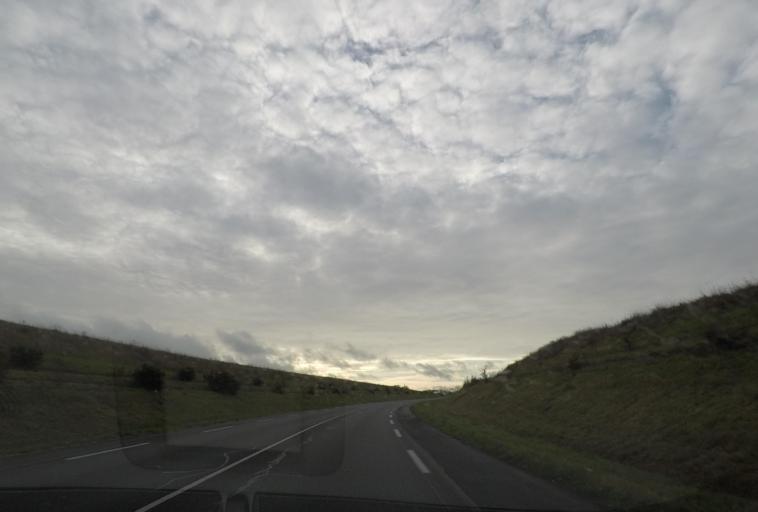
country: FR
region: Pays de la Loire
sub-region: Departement de la Sarthe
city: Saint-Calais
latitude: 47.9325
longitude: 0.7563
